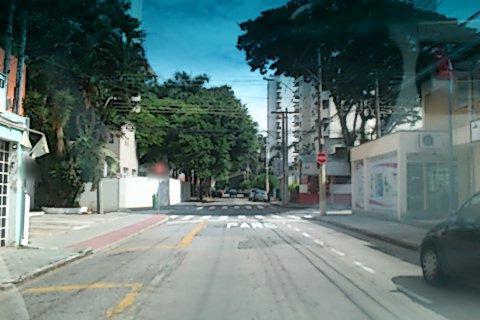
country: BR
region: Sao Paulo
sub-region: Sao Jose Dos Campos
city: Sao Jose dos Campos
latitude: -23.2005
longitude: -45.8938
